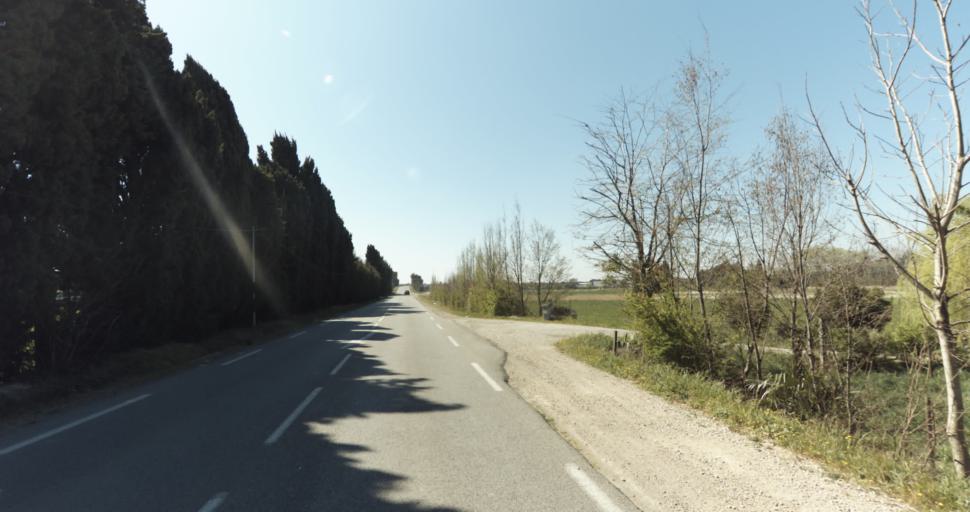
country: FR
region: Provence-Alpes-Cote d'Azur
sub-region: Departement des Bouches-du-Rhone
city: Pelissanne
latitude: 43.6200
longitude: 5.1428
